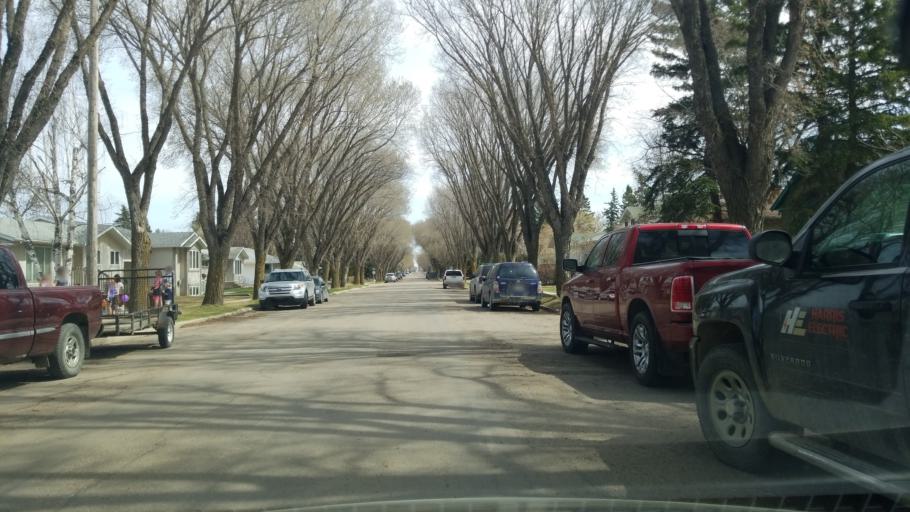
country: CA
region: Saskatchewan
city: Lloydminster
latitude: 53.2816
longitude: -110.0197
